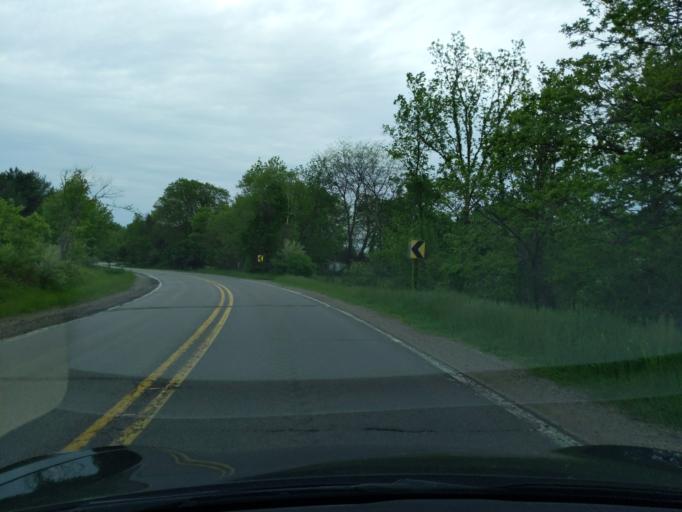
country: US
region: Michigan
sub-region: Ingham County
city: Mason
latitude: 42.6180
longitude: -84.3598
